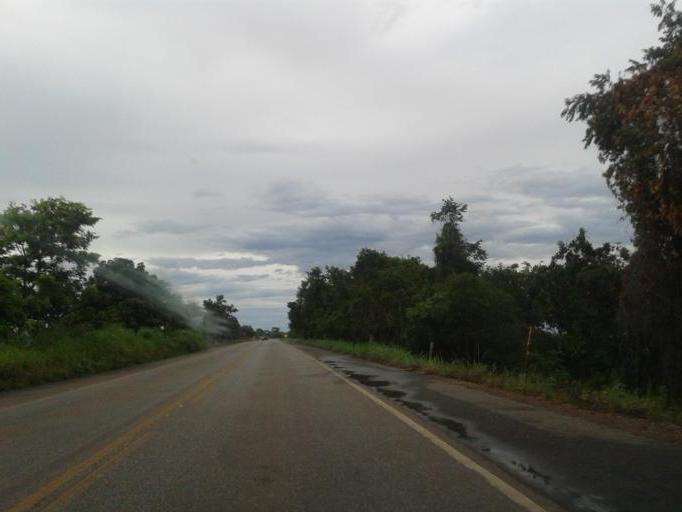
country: BR
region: Goias
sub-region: Mozarlandia
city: Mozarlandia
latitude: -14.8025
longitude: -50.5339
